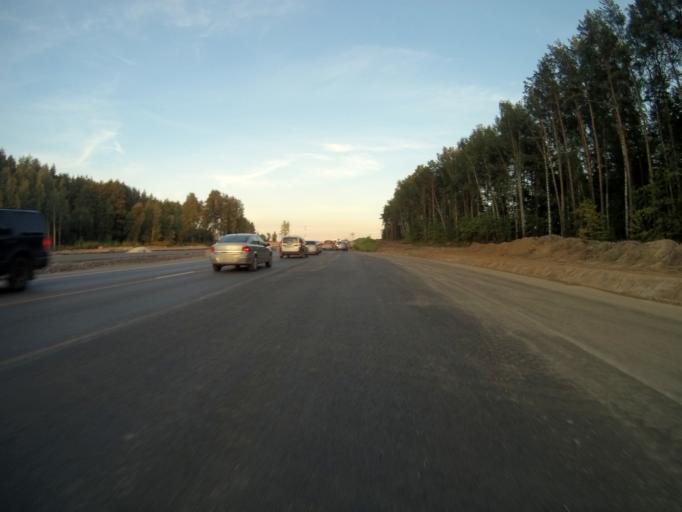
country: RU
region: Vladimir
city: Kommunar
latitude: 56.0741
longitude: 40.4850
